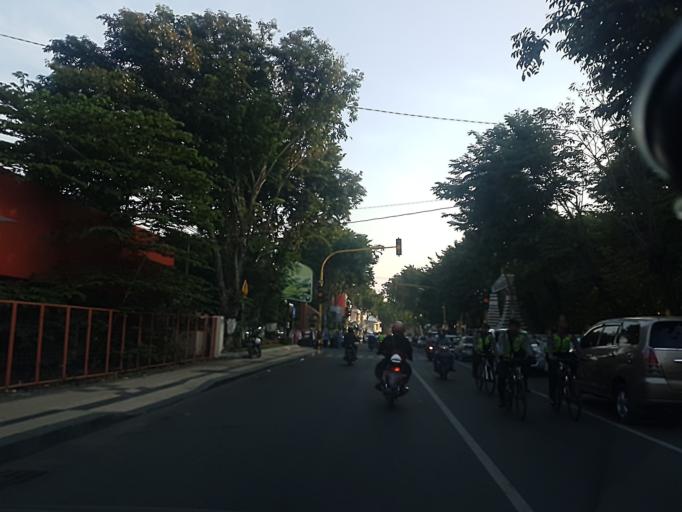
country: ID
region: East Java
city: Gresik
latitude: -7.1606
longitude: 112.6552
